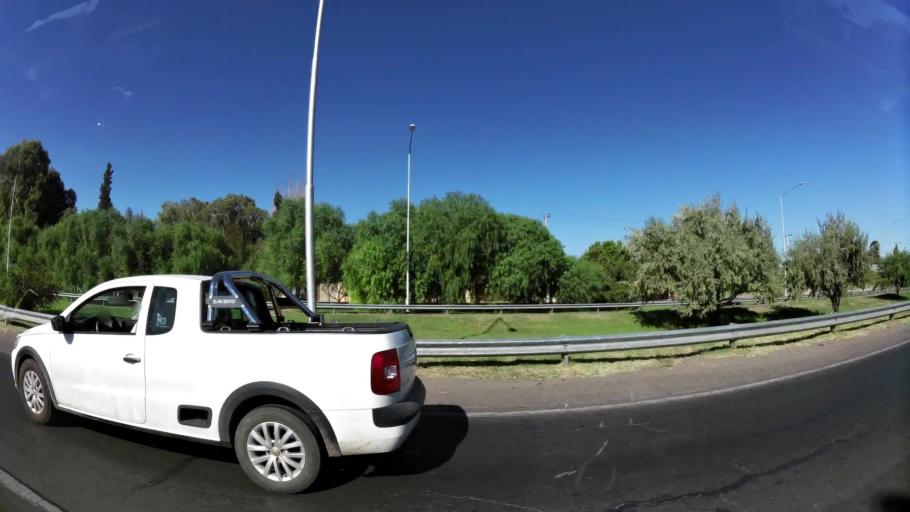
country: AR
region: San Juan
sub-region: Departamento de Santa Lucia
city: Santa Lucia
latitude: -31.5308
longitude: -68.5039
